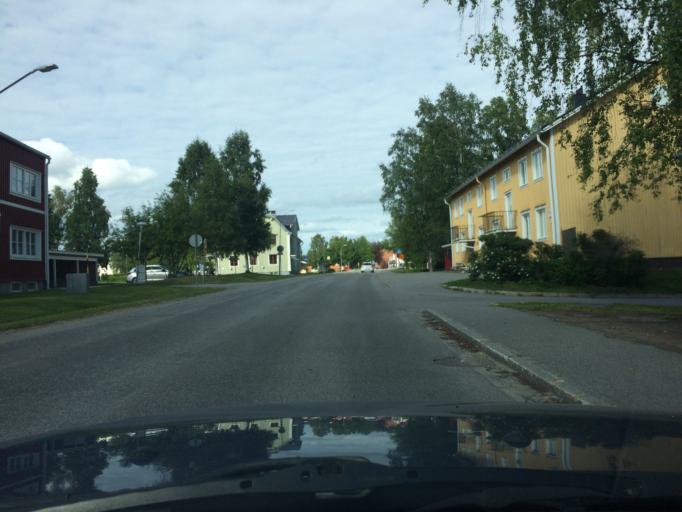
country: SE
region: Norrbotten
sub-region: Pitea Kommun
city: Bergsviken
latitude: 65.3442
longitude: 21.3987
